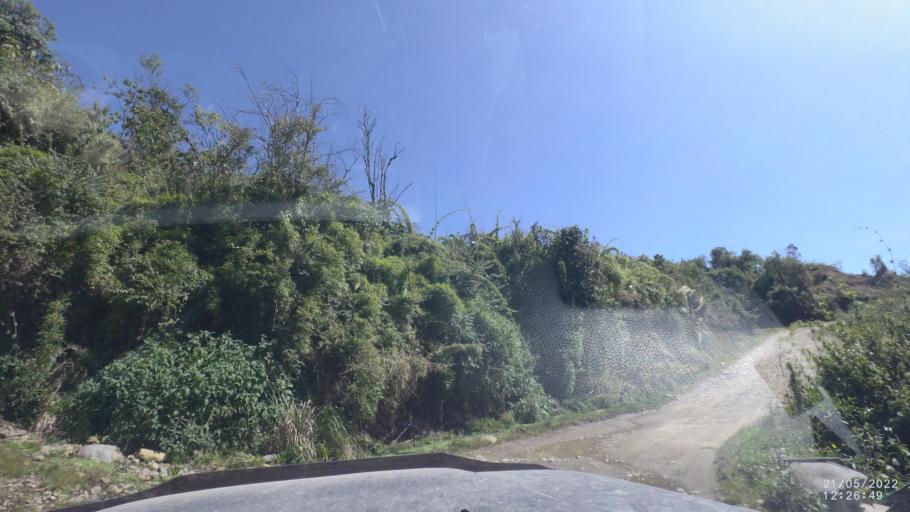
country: BO
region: Cochabamba
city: Colomi
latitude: -17.2198
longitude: -65.9112
